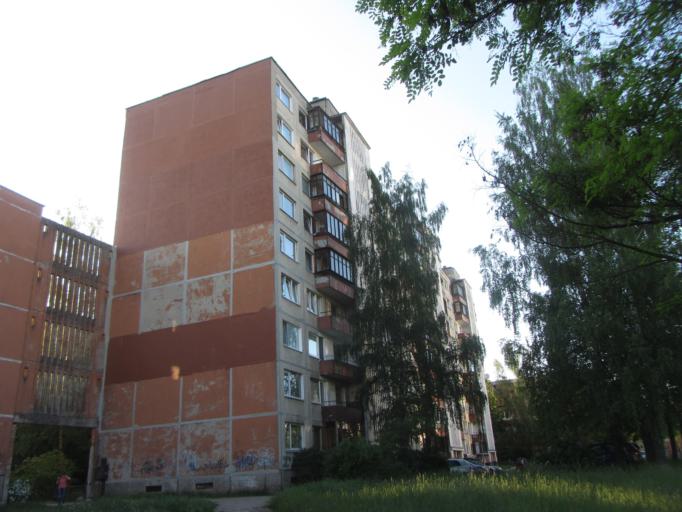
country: LT
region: Vilnius County
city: Seskine
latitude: 54.7275
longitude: 25.2726
